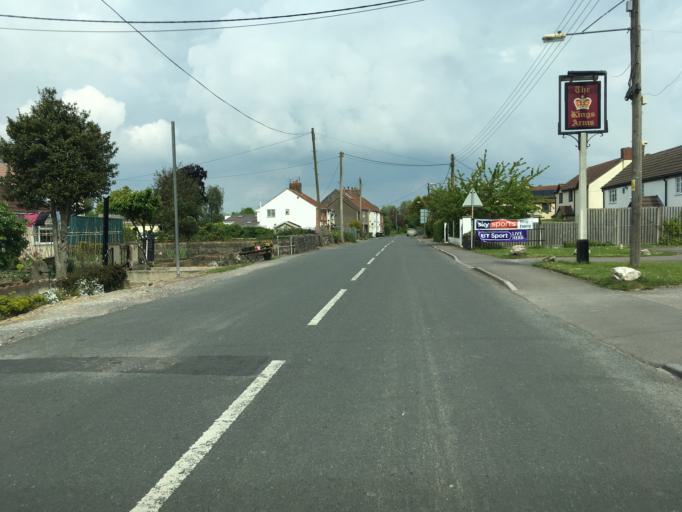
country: GB
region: England
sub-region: South Gloucestershire
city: Severn Beach
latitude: 51.5660
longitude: -2.6486
